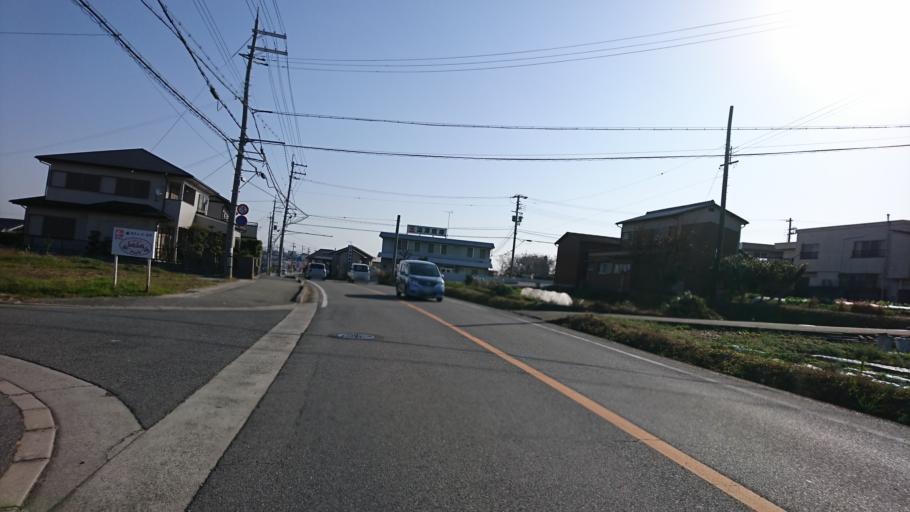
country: JP
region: Hyogo
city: Kakogawacho-honmachi
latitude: 34.7632
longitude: 134.8813
